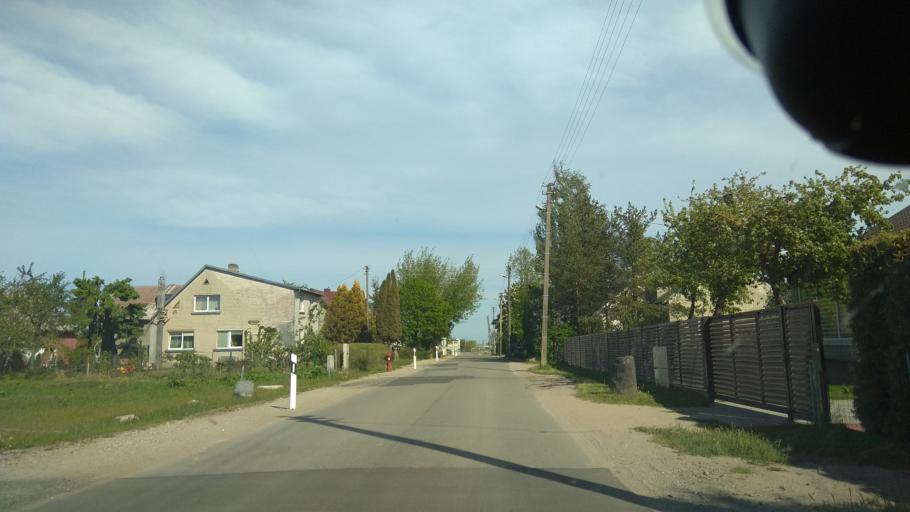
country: LT
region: Klaipedos apskritis
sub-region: Klaipeda
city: Klaipeda
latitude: 55.7564
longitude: 21.1893
